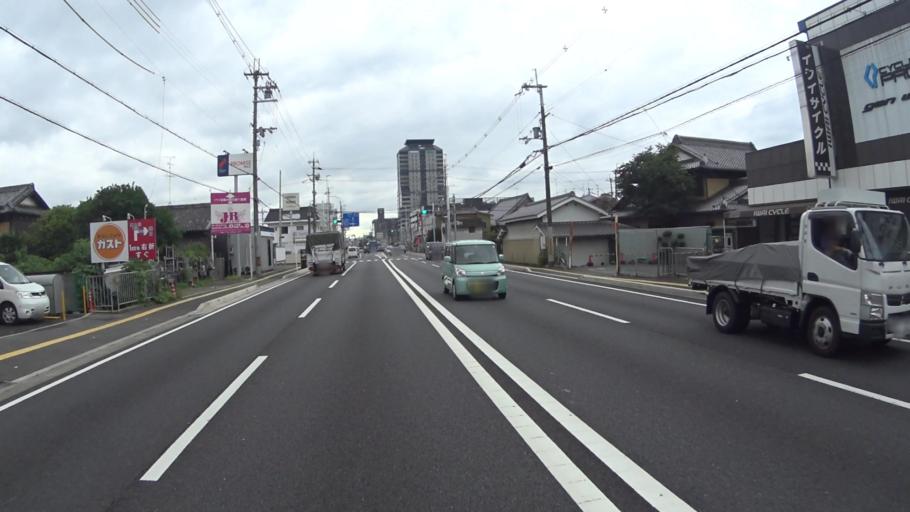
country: JP
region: Kyoto
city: Muko
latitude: 34.9563
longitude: 135.7168
